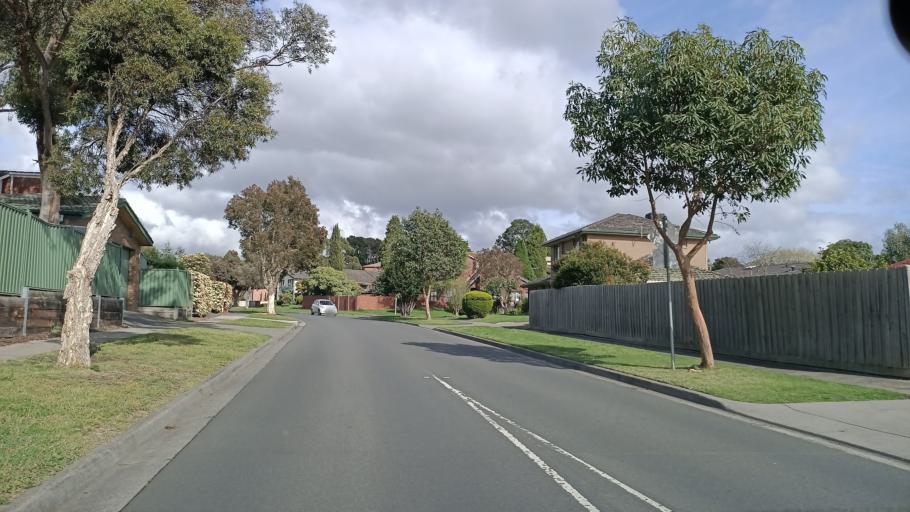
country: AU
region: Victoria
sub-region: Monash
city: Mulgrave
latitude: -37.9253
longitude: 145.2014
